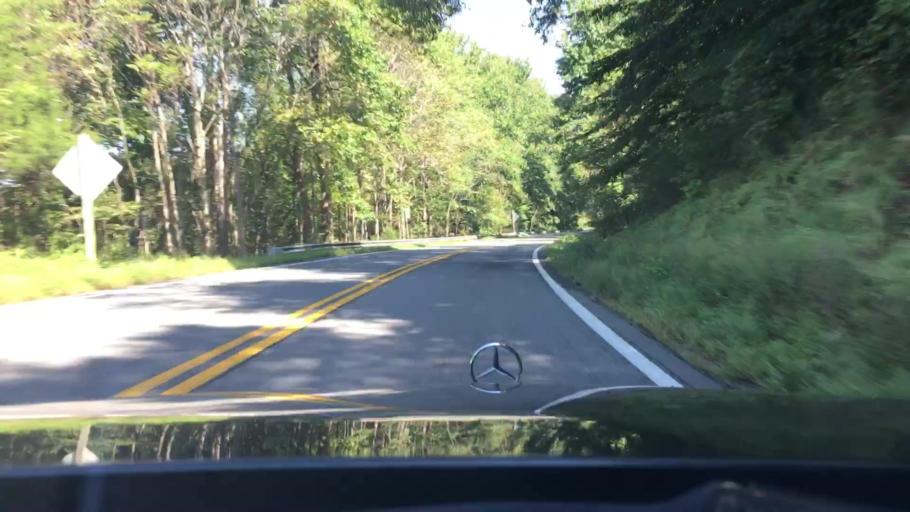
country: US
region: Virginia
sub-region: Nelson County
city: Nellysford
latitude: 37.8710
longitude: -78.8206
